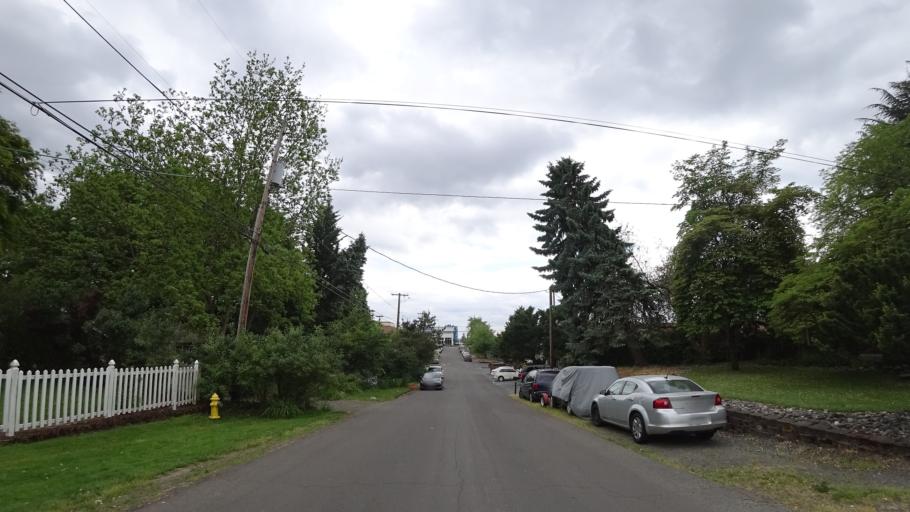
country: US
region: Oregon
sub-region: Washington County
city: Cedar Hills
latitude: 45.4934
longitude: -122.7874
